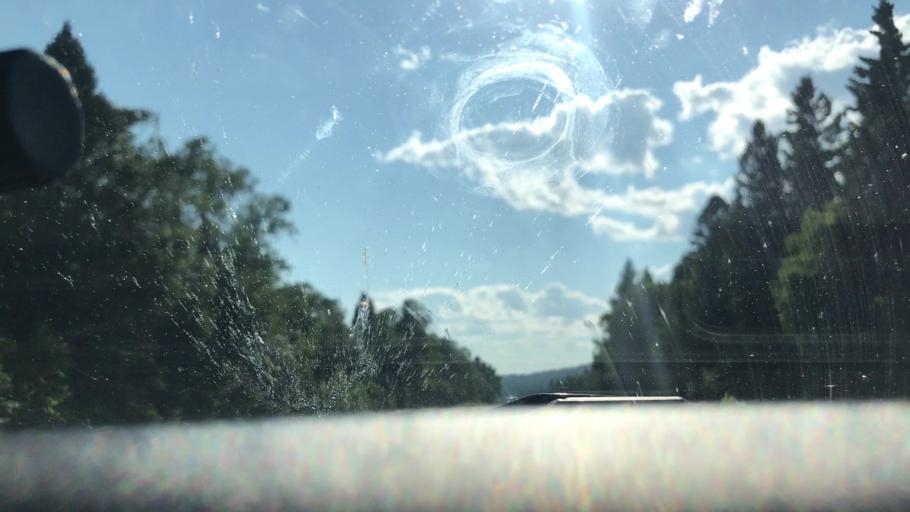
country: US
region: Minnesota
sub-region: Cook County
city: Grand Marais
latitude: 47.7956
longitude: -90.1384
